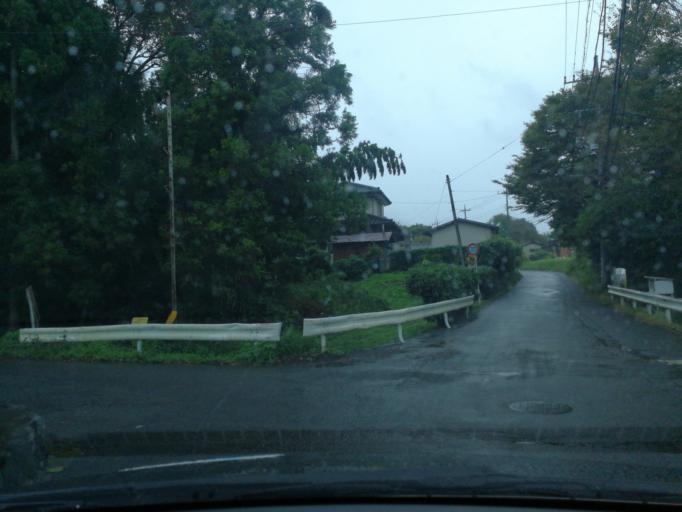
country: JP
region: Tokyo
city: Hachioji
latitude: 35.5925
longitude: 139.2337
